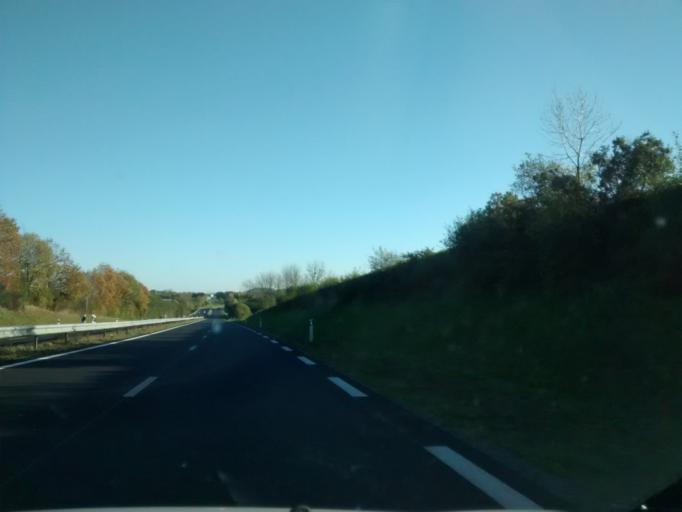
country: FR
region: Brittany
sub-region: Departement des Cotes-d'Armor
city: Pedernec
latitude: 48.6000
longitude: -3.2674
